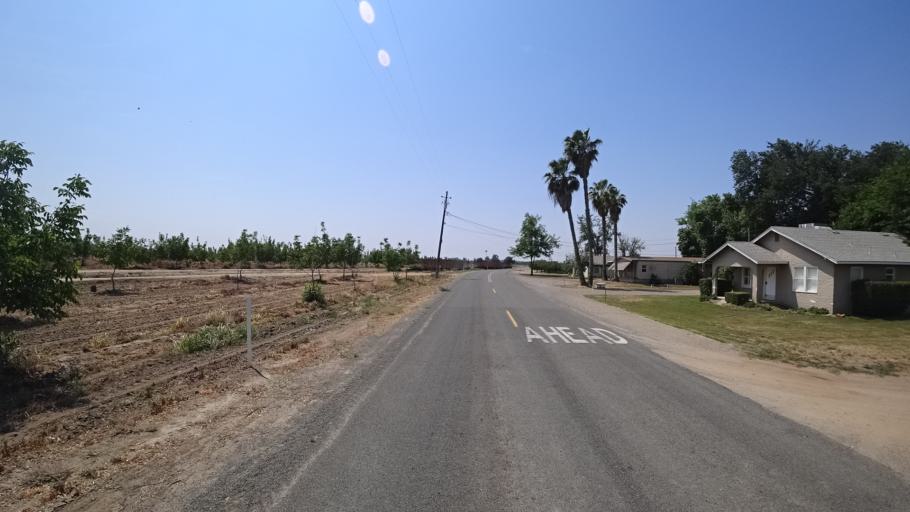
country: US
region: California
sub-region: Kings County
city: Lemoore
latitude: 36.3298
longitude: -119.7628
